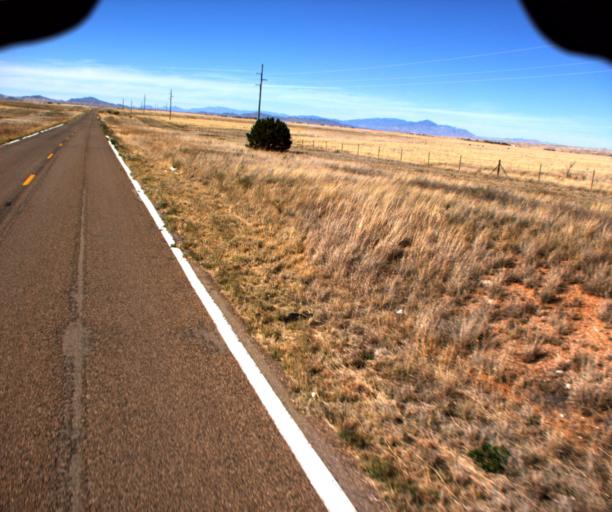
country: US
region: Arizona
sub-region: Cochise County
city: Huachuca City
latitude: 31.6339
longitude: -110.5966
